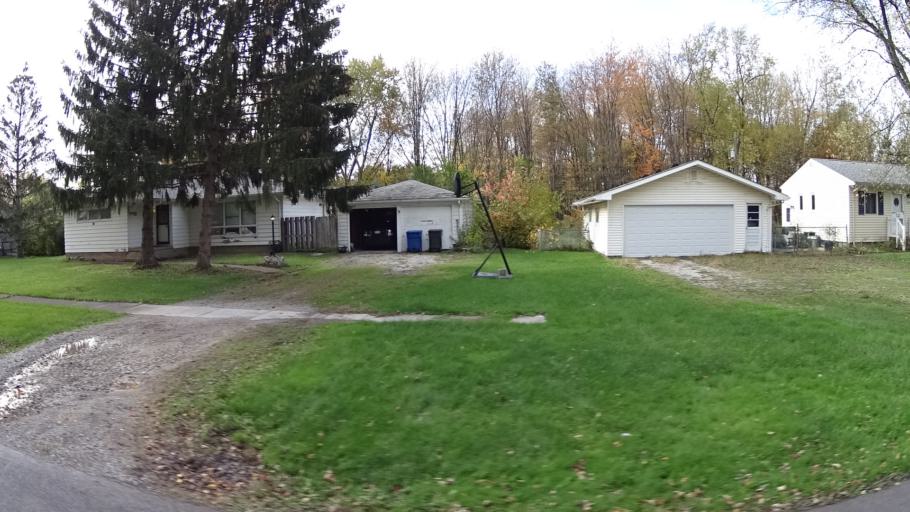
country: US
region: Ohio
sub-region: Lorain County
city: Sheffield Lake
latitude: 41.4919
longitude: -82.0920
